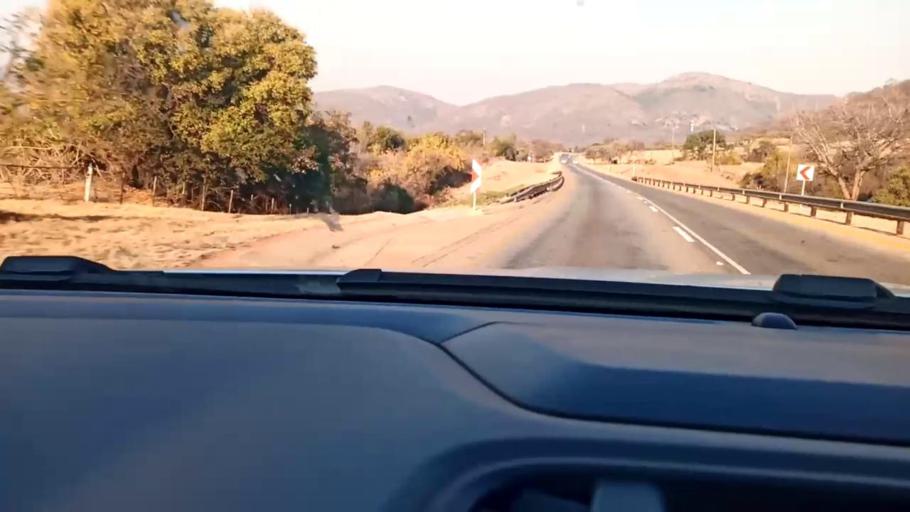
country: ZA
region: Limpopo
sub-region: Mopani District Municipality
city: Duiwelskloof
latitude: -23.6441
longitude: 30.1623
